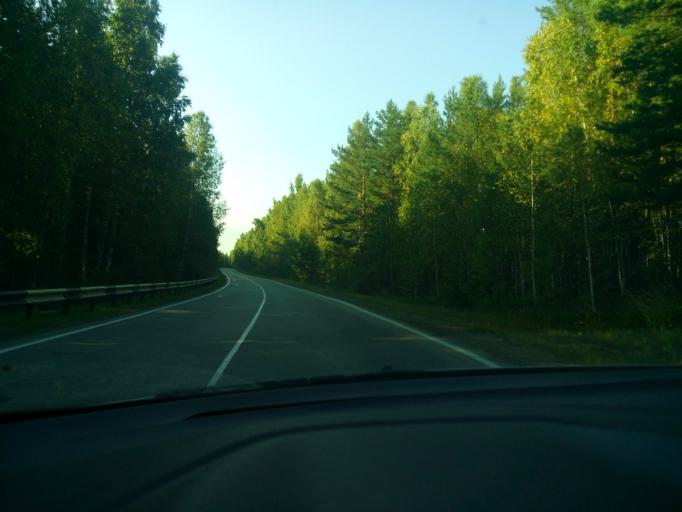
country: RU
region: Chelyabinsk
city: Ozersk
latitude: 55.8496
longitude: 60.6573
